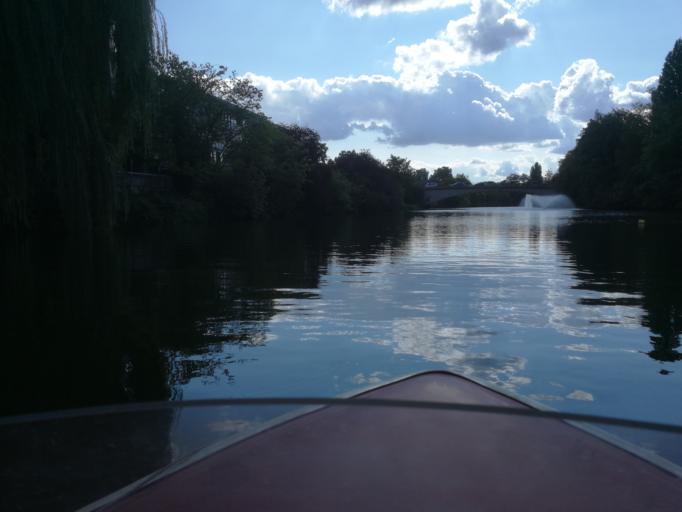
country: FR
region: Centre
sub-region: Departement d'Indre-et-Loire
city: Saint-Avertin
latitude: 47.3694
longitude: 0.7280
